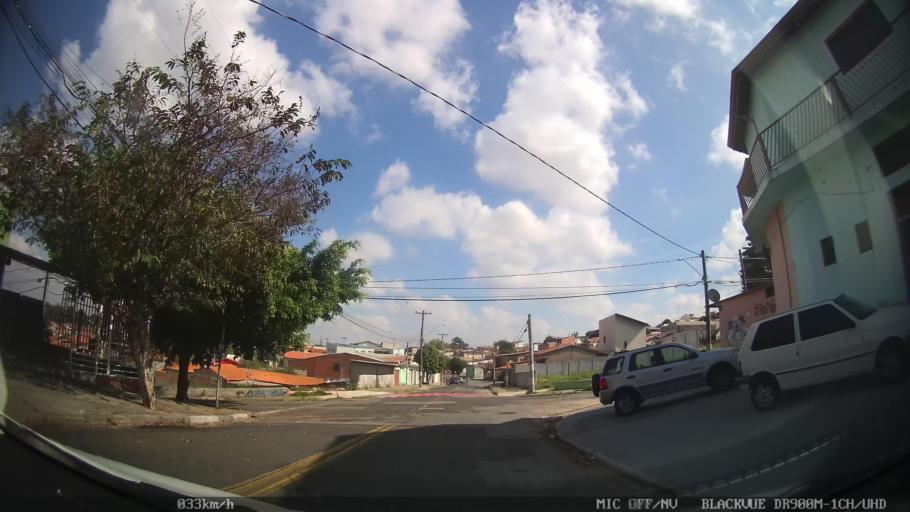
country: BR
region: Sao Paulo
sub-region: Campinas
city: Campinas
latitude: -22.9374
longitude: -47.1145
